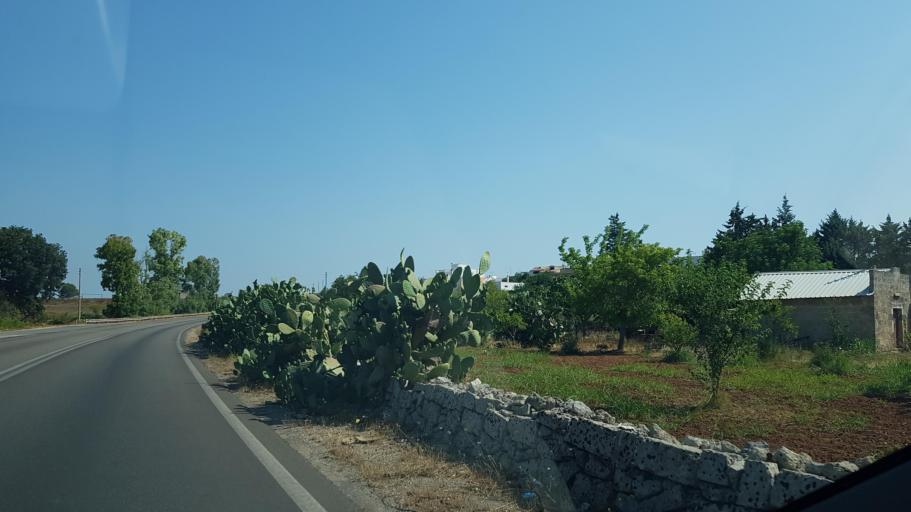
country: IT
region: Apulia
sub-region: Provincia di Lecce
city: Nociglia
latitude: 40.0389
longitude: 18.3210
